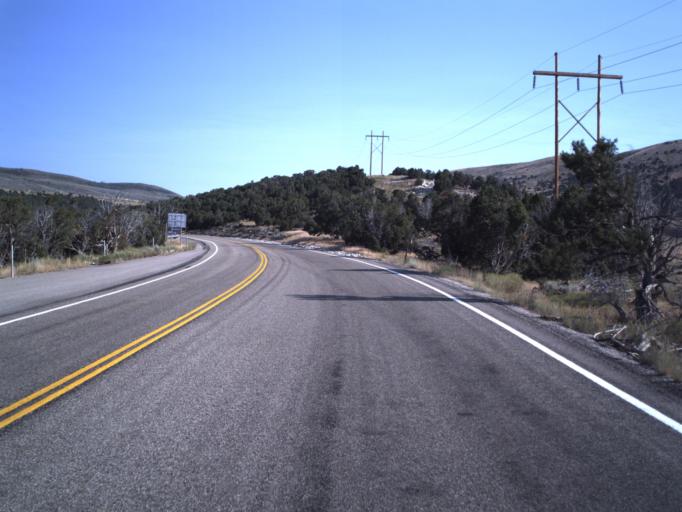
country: US
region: Utah
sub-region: Uintah County
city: Vernal
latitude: 40.6367
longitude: -109.4795
